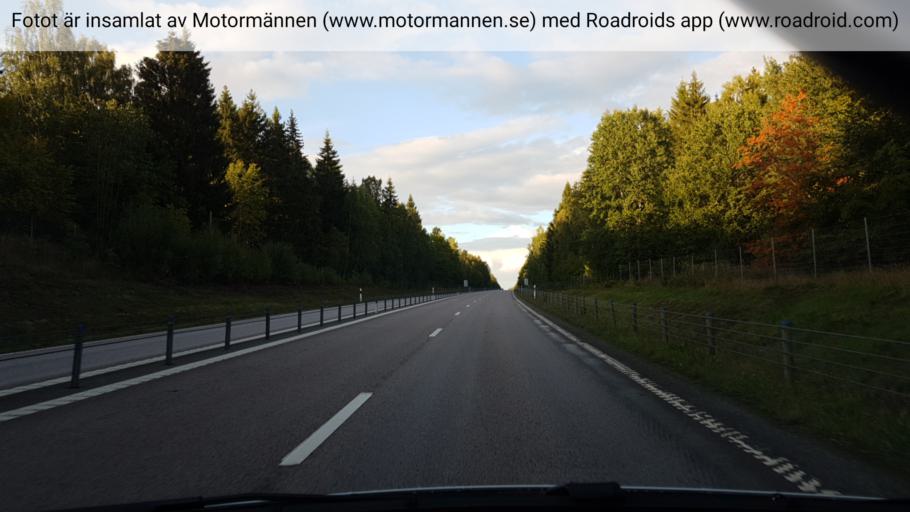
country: SE
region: Vaestra Goetaland
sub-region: Mariestads Kommun
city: Mariestad
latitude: 58.5999
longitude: 13.7994
